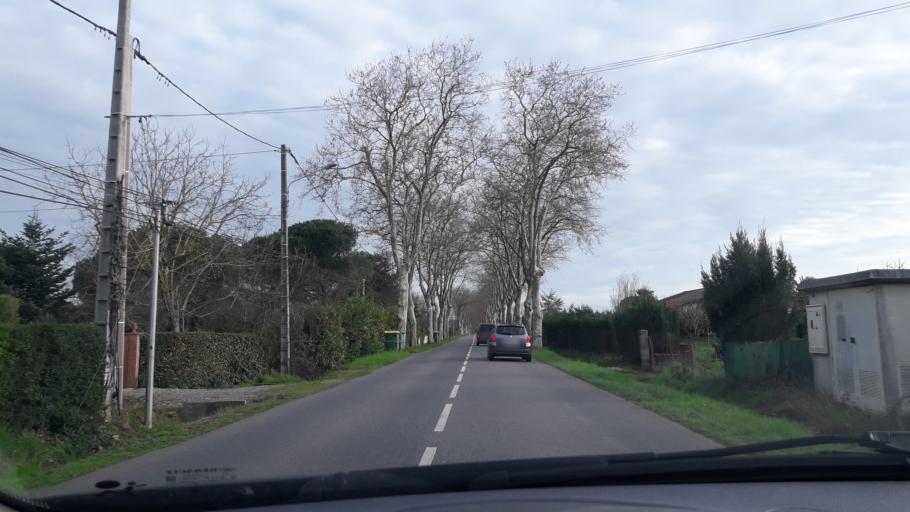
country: FR
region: Midi-Pyrenees
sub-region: Departement de la Haute-Garonne
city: Grenade
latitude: 43.7614
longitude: 1.2904
